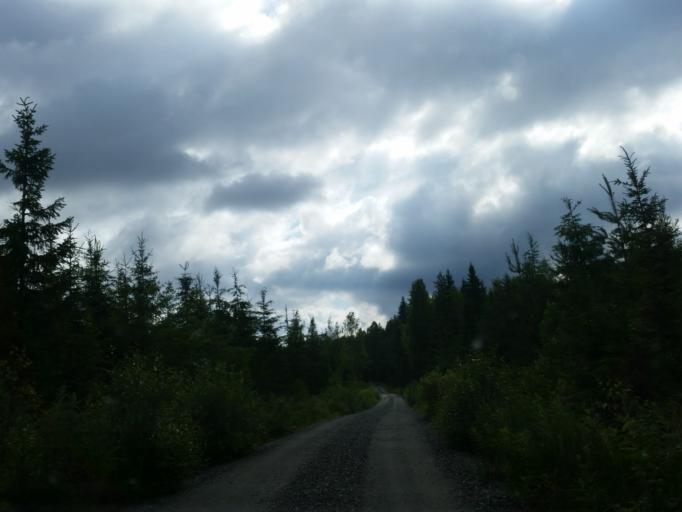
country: FI
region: Northern Savo
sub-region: Sisae-Savo
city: Tervo
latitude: 63.0562
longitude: 26.6724
